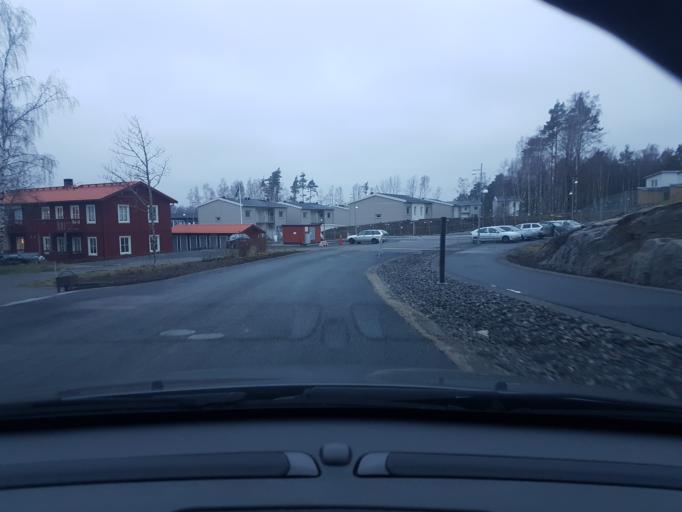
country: SE
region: Vaestra Goetaland
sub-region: Ale Kommun
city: Alvangen
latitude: 57.9480
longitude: 12.1217
